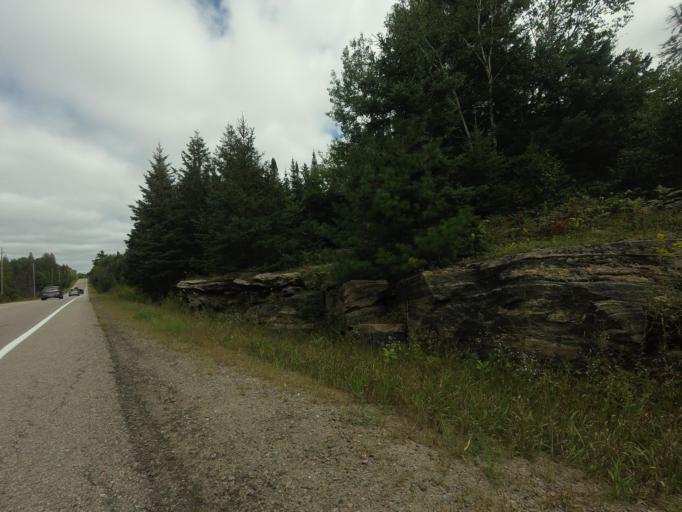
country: CA
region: Ontario
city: Bancroft
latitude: 44.9013
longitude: -78.4352
